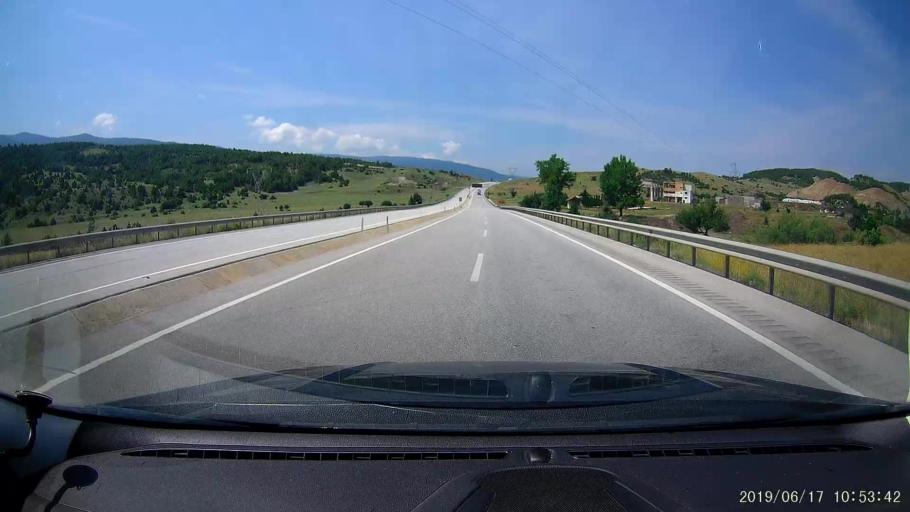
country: TR
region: Corum
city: Hacihamza
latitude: 41.0804
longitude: 34.3155
